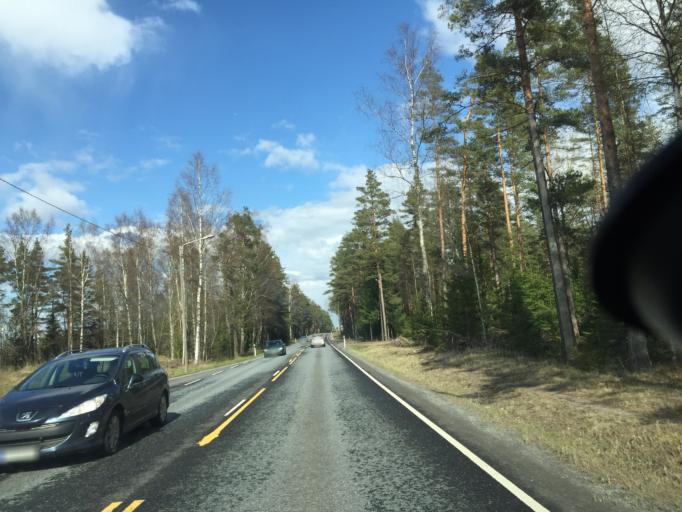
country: FI
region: Uusimaa
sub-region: Raaseporin
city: Karis
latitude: 60.1103
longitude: 23.7922
